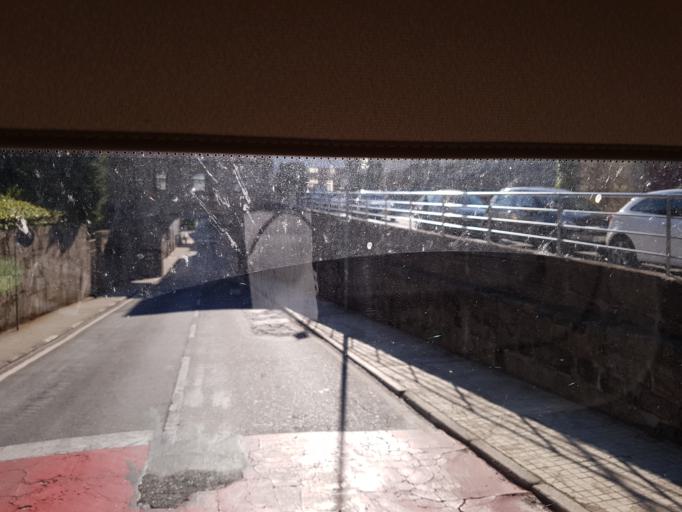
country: PT
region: Castelo Branco
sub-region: Covilha
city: Covilha
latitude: 40.2777
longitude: -7.5073
